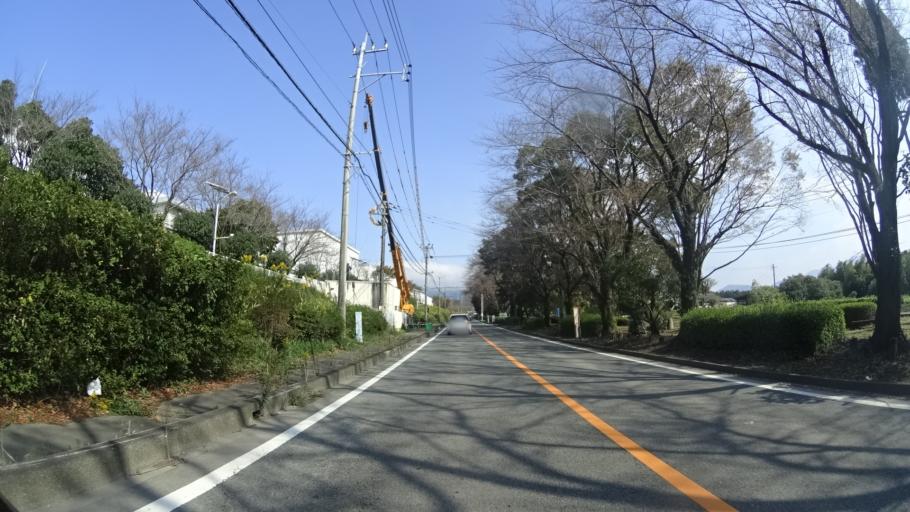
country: JP
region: Kumamoto
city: Ozu
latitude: 32.8937
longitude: 130.9157
